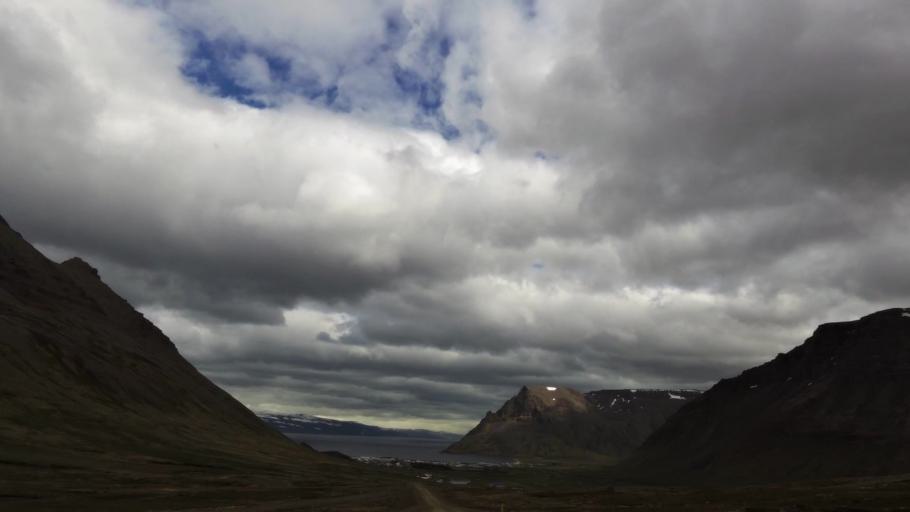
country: IS
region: Westfjords
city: Isafjoerdur
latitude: 66.1619
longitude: -23.3102
